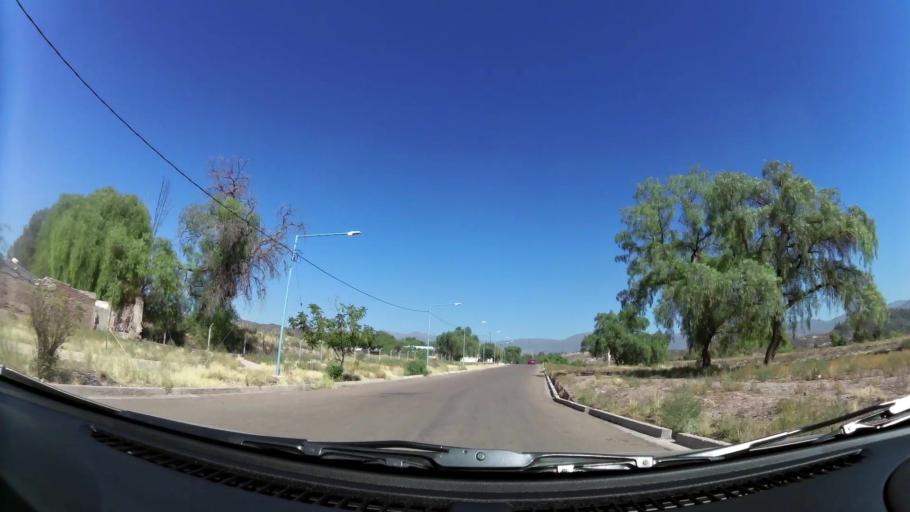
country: AR
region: Mendoza
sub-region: Departamento de Godoy Cruz
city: Godoy Cruz
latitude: -32.9003
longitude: -68.8782
